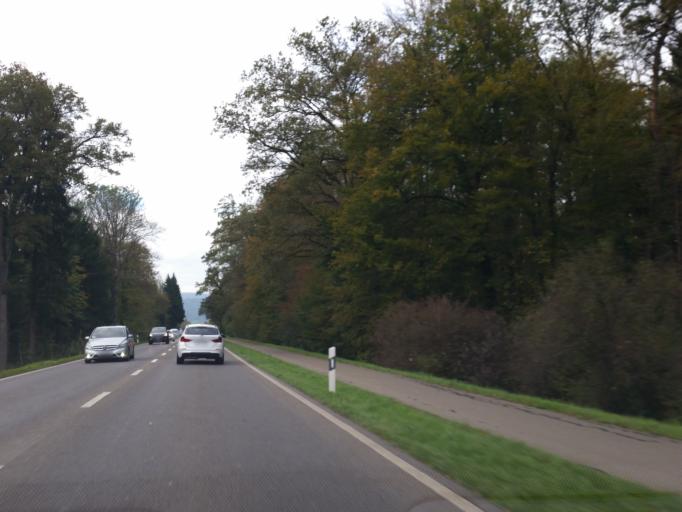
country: CH
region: Zurich
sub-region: Bezirk Dielsdorf
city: Regensdorf
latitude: 47.4335
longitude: 8.4811
